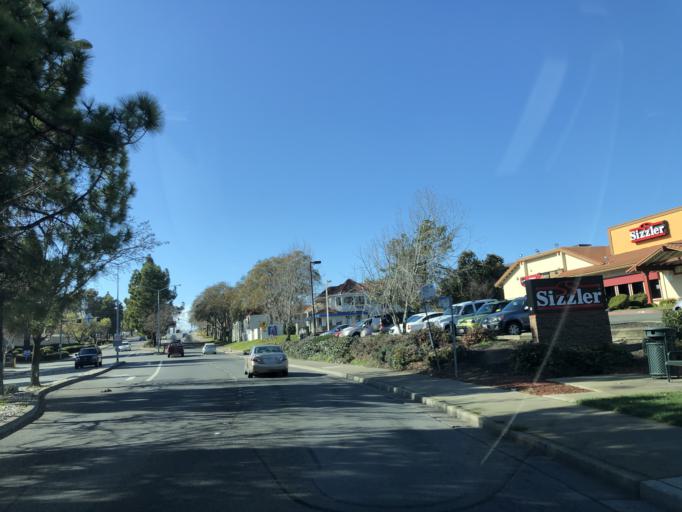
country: US
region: California
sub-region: Contra Costa County
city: Tara Hills
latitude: 37.9918
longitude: -122.3035
